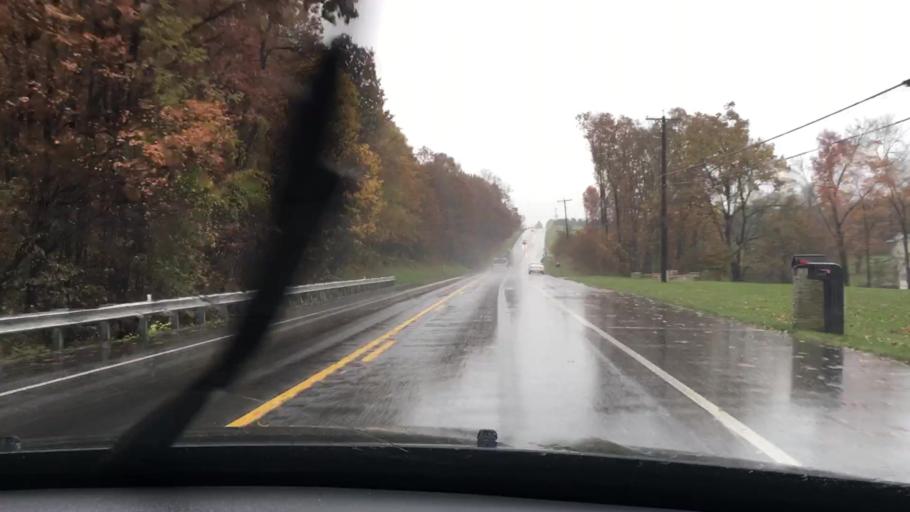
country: US
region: Maryland
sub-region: Carroll County
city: New Windsor
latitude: 39.4956
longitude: -77.0558
